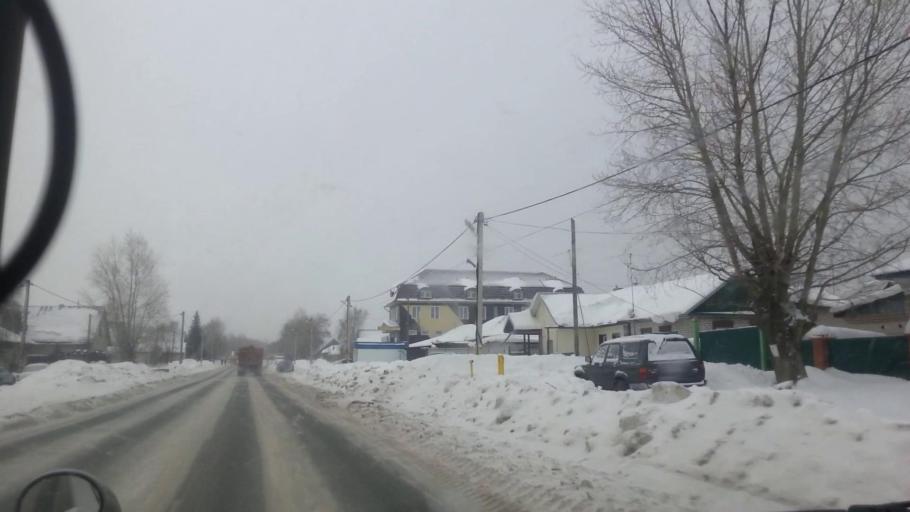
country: RU
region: Altai Krai
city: Vlasikha
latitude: 53.2980
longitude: 83.5868
